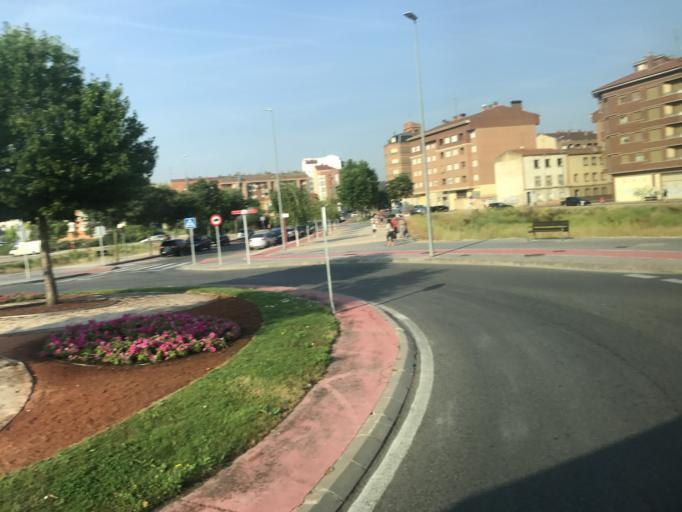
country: ES
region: Castille and Leon
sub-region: Provincia de Burgos
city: Miranda de Ebro
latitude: 42.6896
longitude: -2.9344
